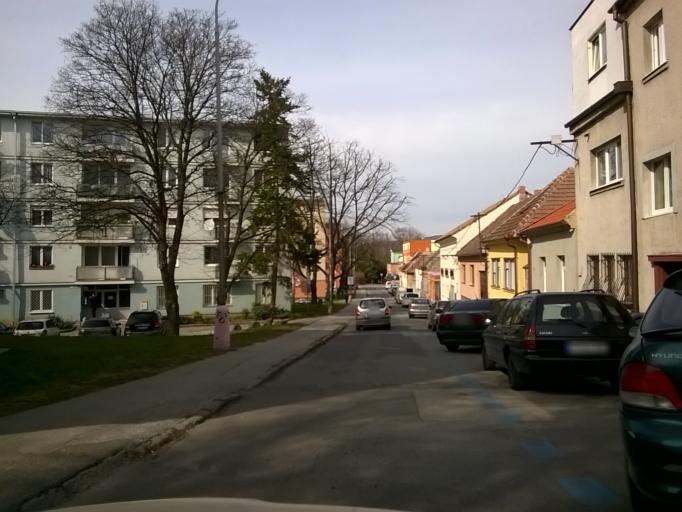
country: SK
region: Nitriansky
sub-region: Okres Nitra
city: Nitra
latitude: 48.3145
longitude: 18.0836
